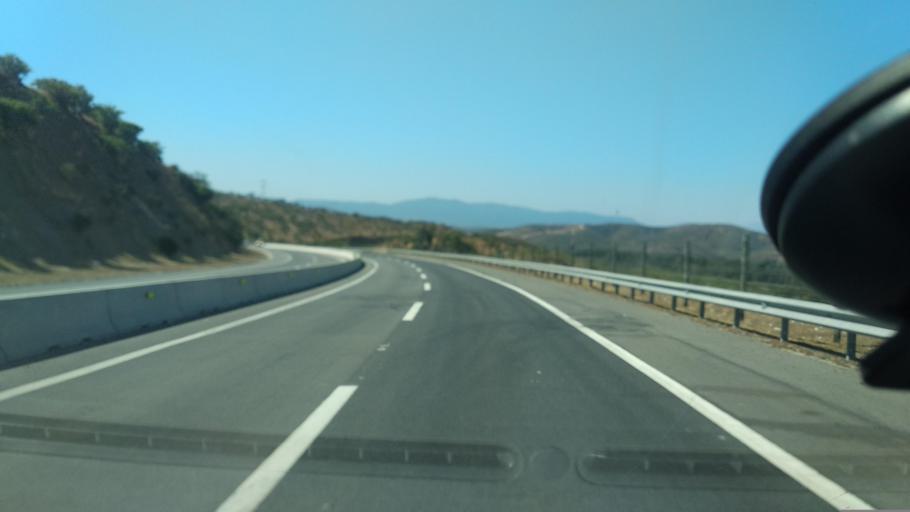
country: CL
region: Valparaiso
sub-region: Provincia de Marga Marga
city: Villa Alemana
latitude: -33.0348
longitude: -71.3189
